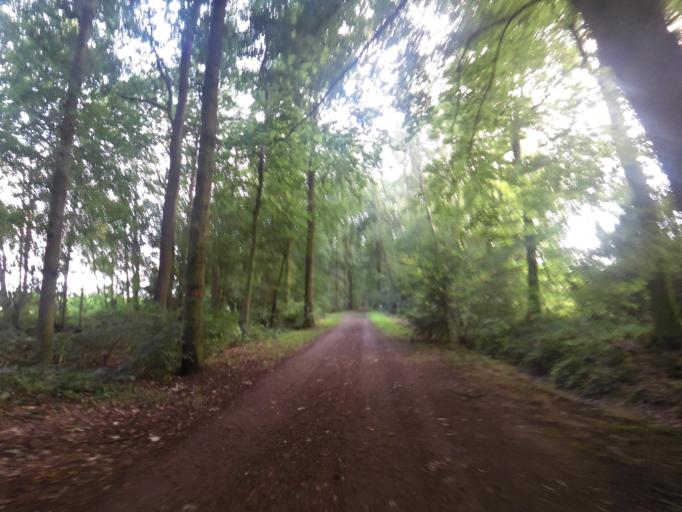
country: NL
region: Gelderland
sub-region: Oude IJsselstreek
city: Gendringen
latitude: 51.8514
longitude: 6.4076
